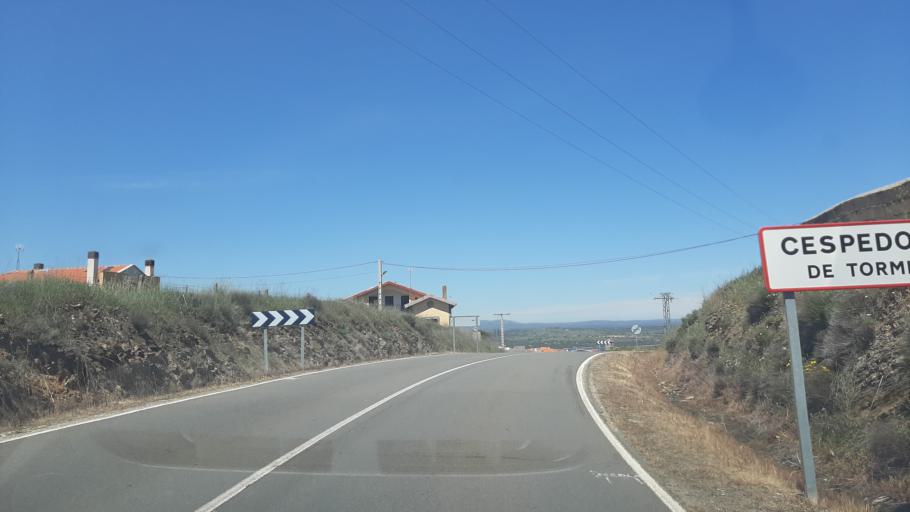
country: ES
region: Castille and Leon
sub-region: Provincia de Salamanca
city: Salvatierra de Tormes
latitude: 40.5396
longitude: -5.5755
